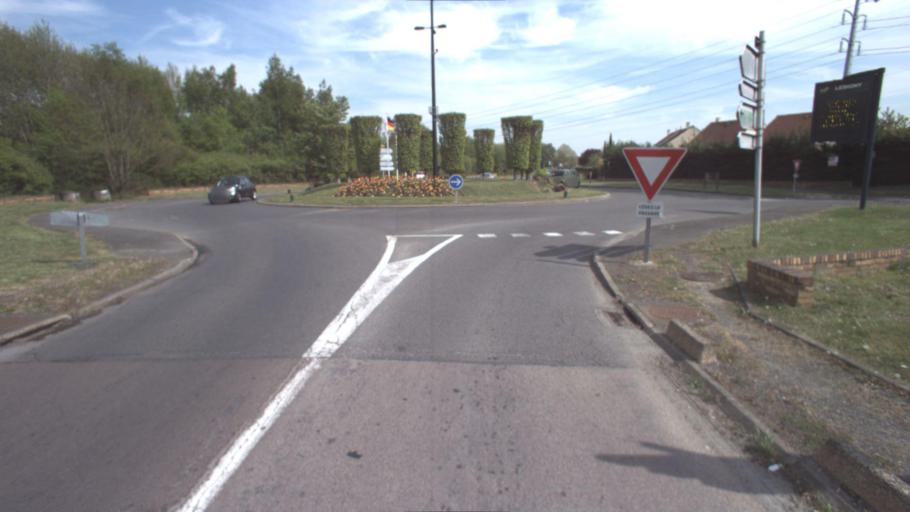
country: FR
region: Ile-de-France
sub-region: Departement de Seine-et-Marne
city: Lesigny
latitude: 48.7487
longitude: 2.6164
